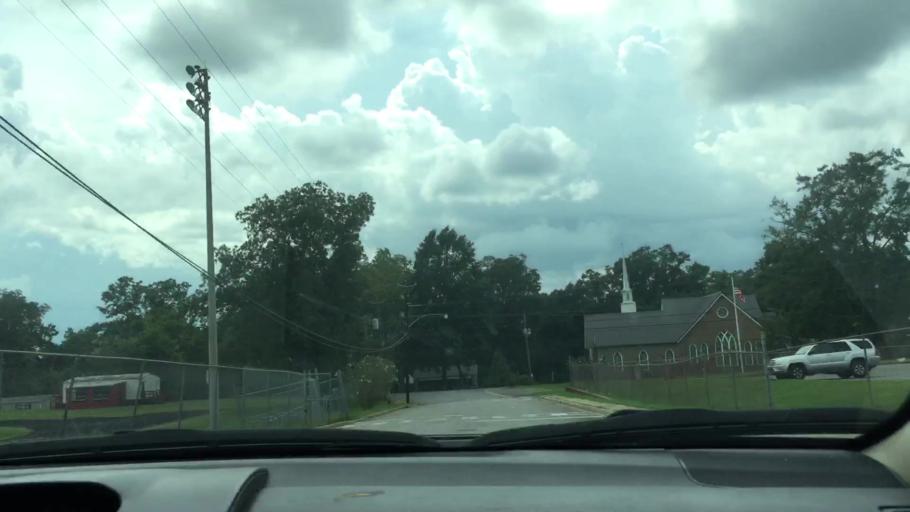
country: US
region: Alabama
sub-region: Hale County
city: Greensboro
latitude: 32.7072
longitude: -87.5878
